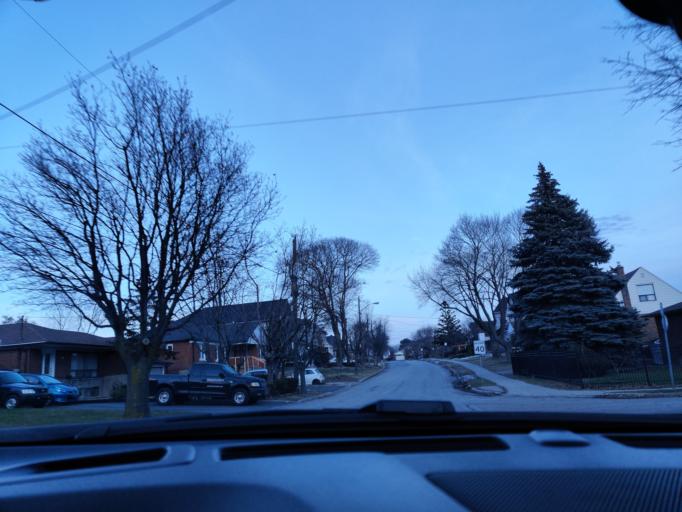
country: CA
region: Ontario
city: Toronto
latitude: 43.7181
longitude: -79.4534
